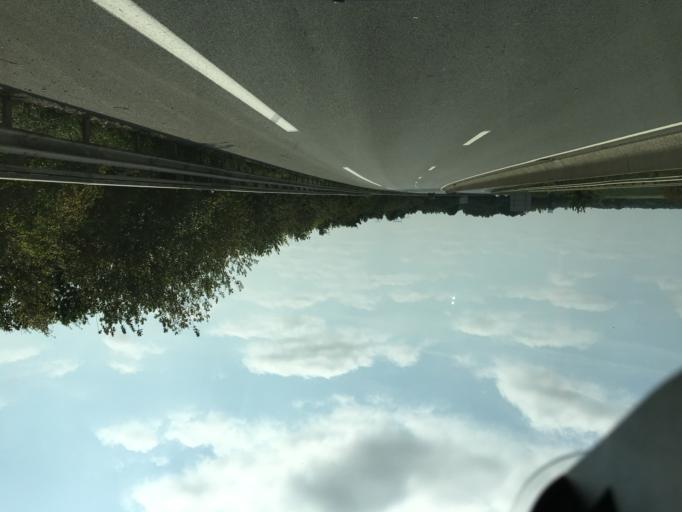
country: FR
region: Nord-Pas-de-Calais
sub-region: Departement du Nord
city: Somain
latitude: 50.3534
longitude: 3.2626
